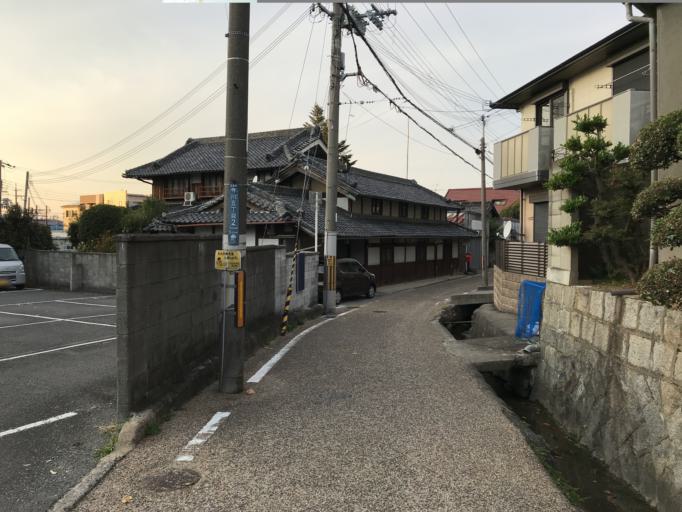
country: JP
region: Osaka
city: Daitocho
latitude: 34.7103
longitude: 135.6444
